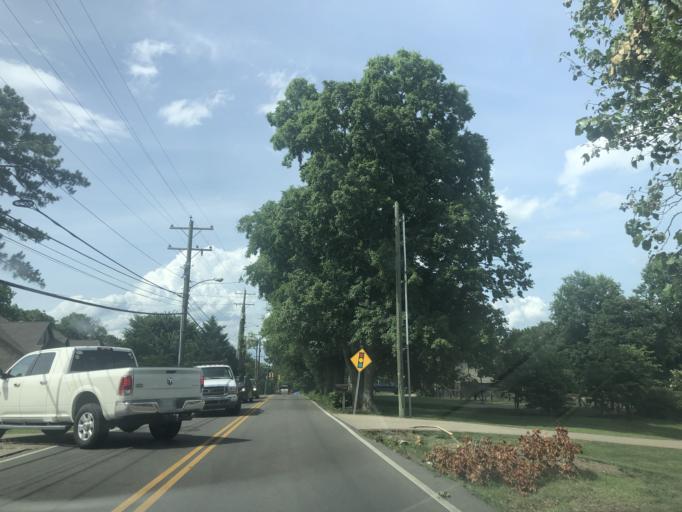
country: US
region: Tennessee
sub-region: Davidson County
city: Oak Hill
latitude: 36.0870
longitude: -86.7911
